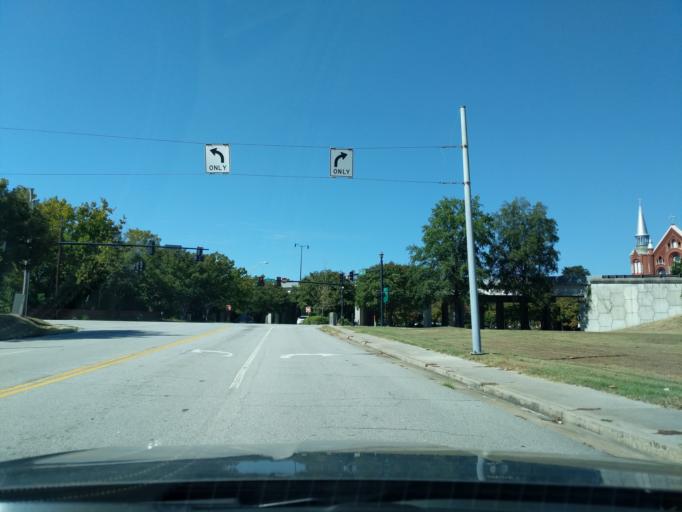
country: US
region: Georgia
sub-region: Richmond County
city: Augusta
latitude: 33.4757
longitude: -81.9762
